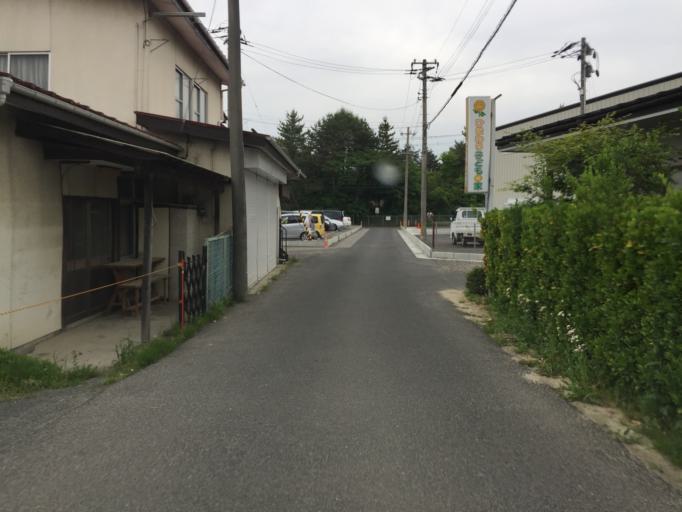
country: JP
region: Fukushima
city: Fukushima-shi
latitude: 37.8013
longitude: 140.4518
